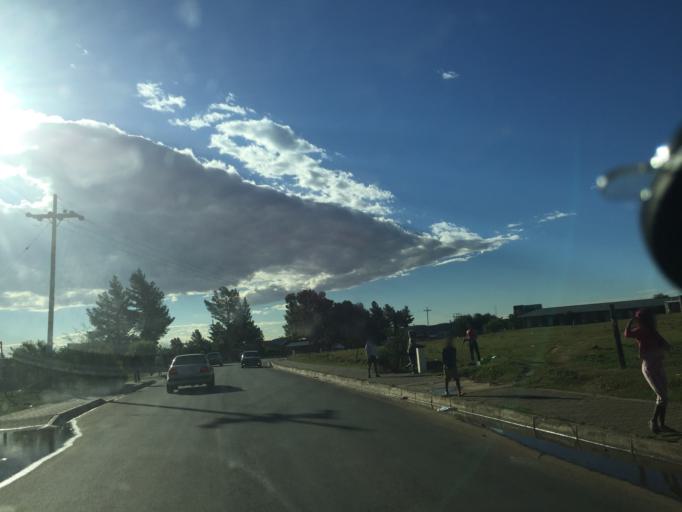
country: LS
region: Maseru
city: Maseru
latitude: -29.2955
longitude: 27.5348
